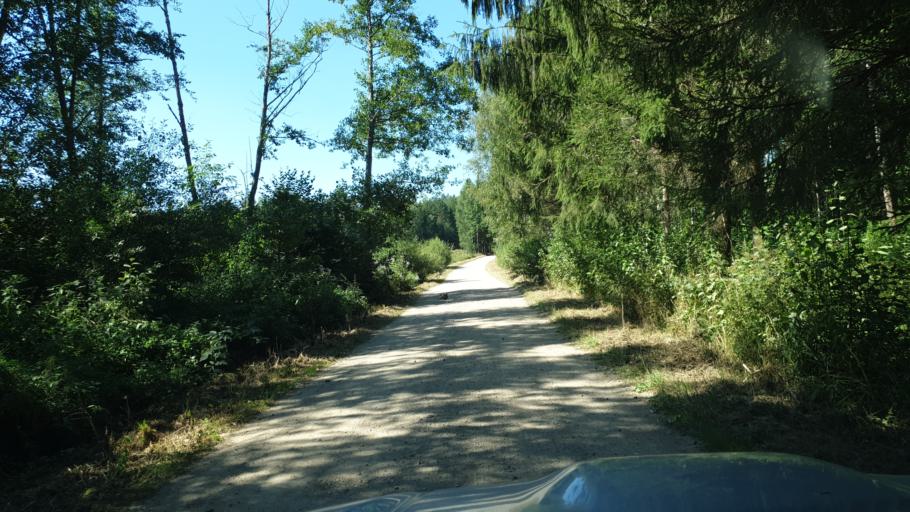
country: LT
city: Sirvintos
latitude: 54.8999
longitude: 24.8959
